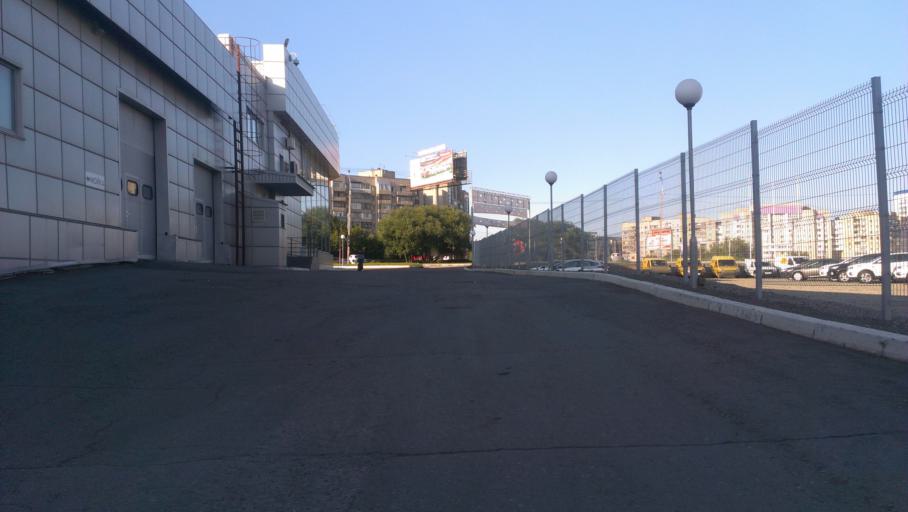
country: RU
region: Altai Krai
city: Novosilikatnyy
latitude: 53.3415
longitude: 83.6914
